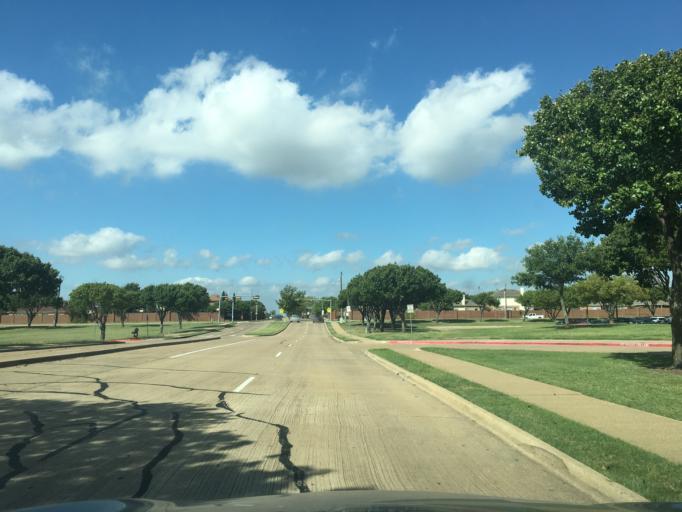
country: US
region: Texas
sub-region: Dallas County
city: Sachse
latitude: 32.9581
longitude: -96.5818
